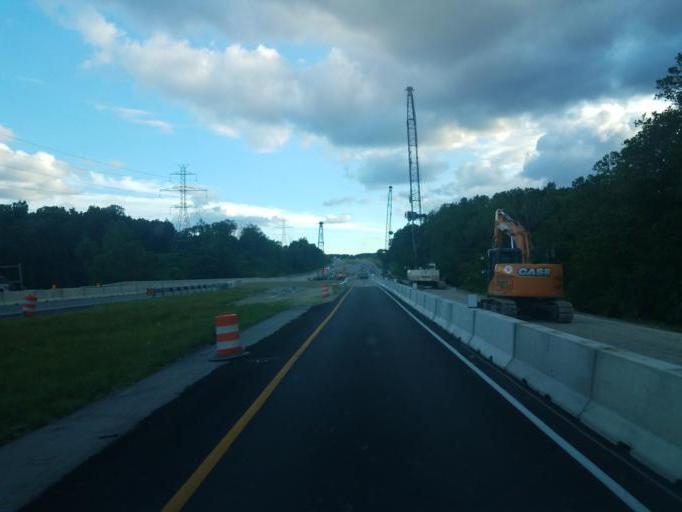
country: US
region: Indiana
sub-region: Allen County
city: Huntertown
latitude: 41.2317
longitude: -85.0973
